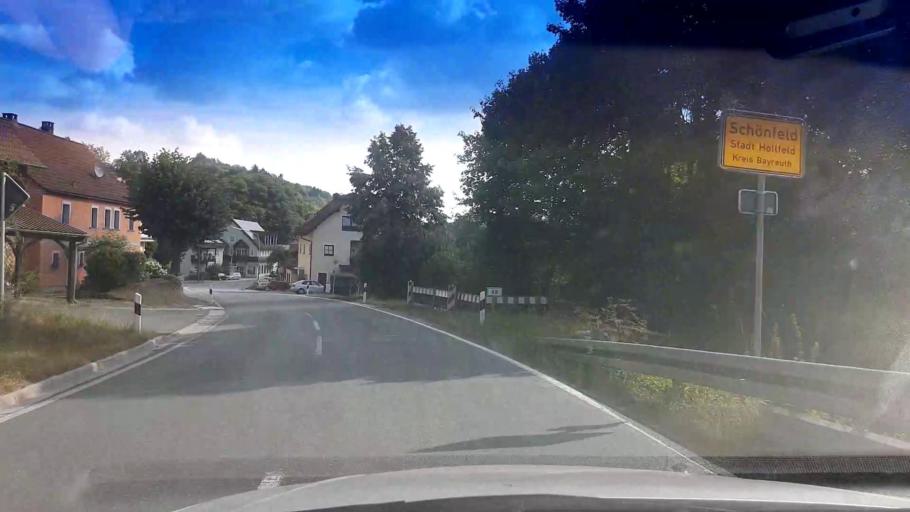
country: DE
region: Bavaria
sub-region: Upper Franconia
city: Plankenfels
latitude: 49.9363
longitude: 11.3631
